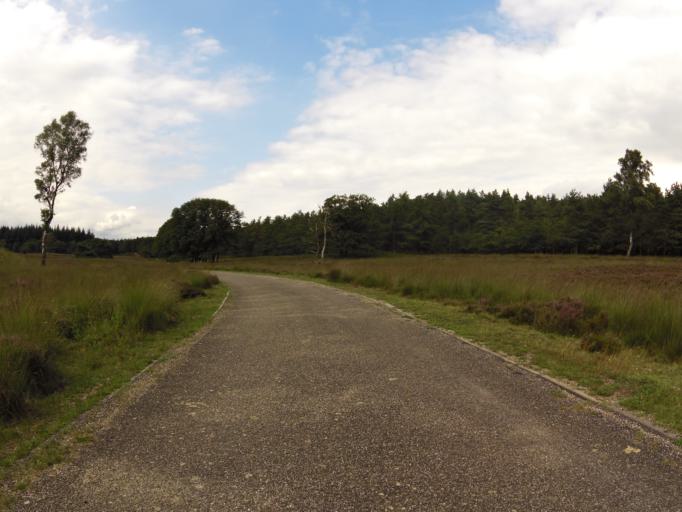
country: NL
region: Gelderland
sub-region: Gemeente Apeldoorn
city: Loenen
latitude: 52.0883
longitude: 5.9770
